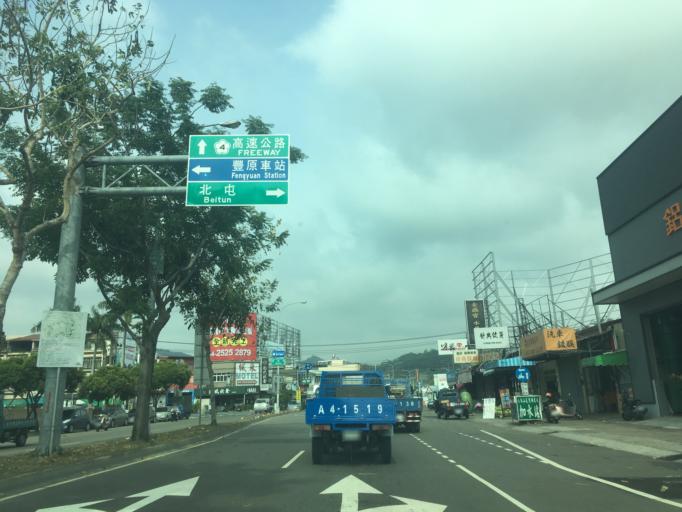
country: TW
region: Taiwan
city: Fengyuan
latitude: 24.2365
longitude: 120.7216
